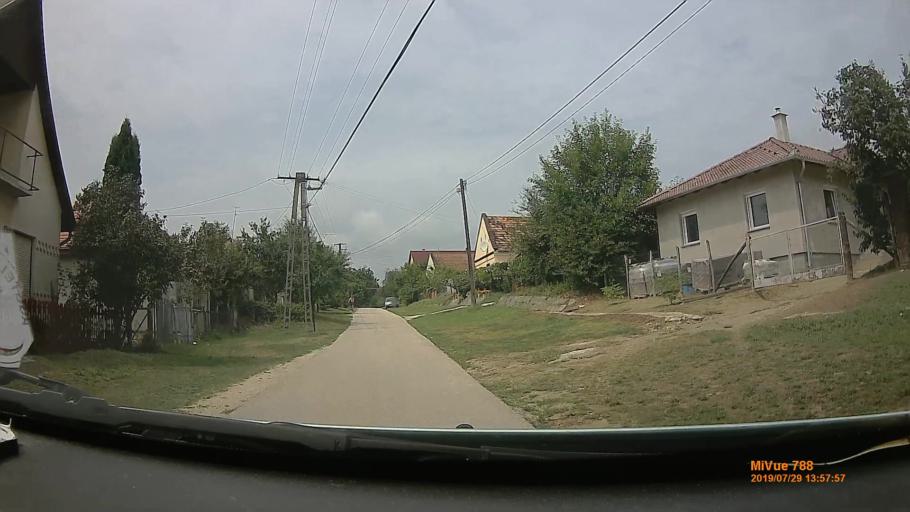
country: HU
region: Somogy
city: Tab
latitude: 46.7786
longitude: 17.9519
